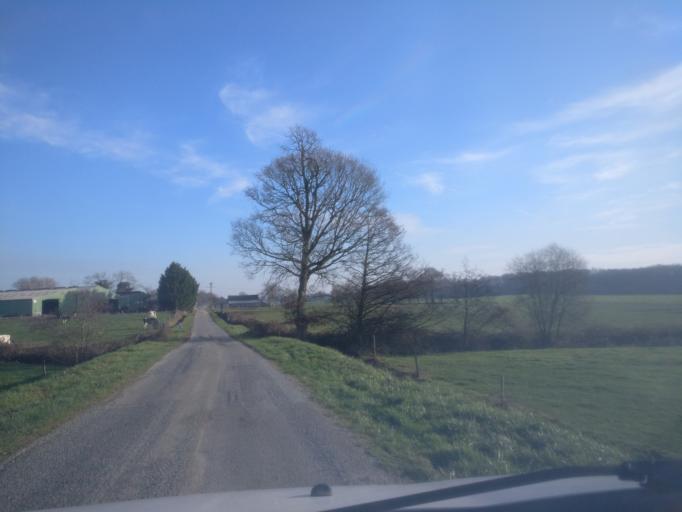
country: FR
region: Brittany
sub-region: Departement d'Ille-et-Vilaine
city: Livre-sur-Changeon
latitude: 48.2190
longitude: -1.3209
